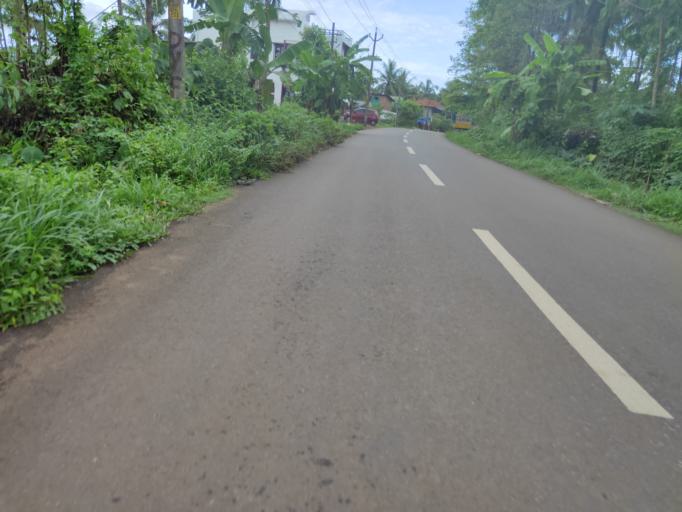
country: IN
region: Kerala
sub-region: Malappuram
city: Manjeri
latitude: 11.1646
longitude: 76.1693
